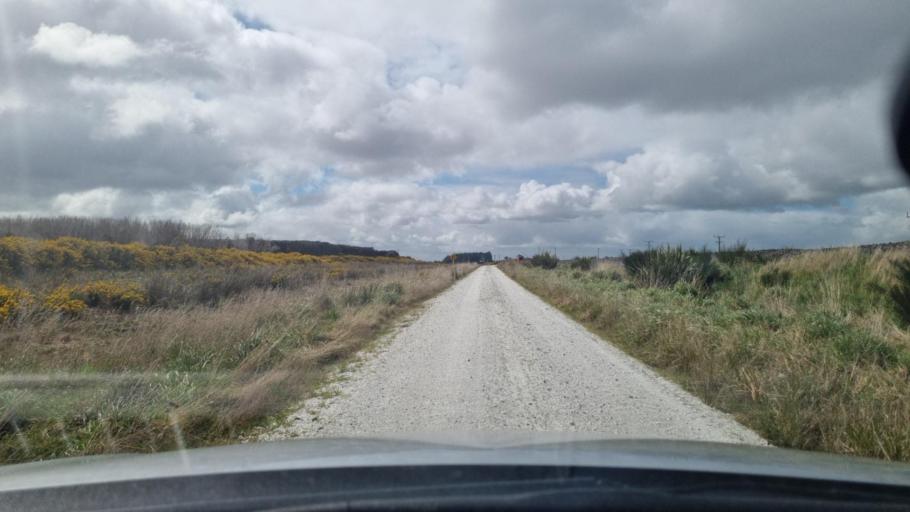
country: NZ
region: Southland
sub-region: Invercargill City
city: Bluff
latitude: -46.5293
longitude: 168.3061
